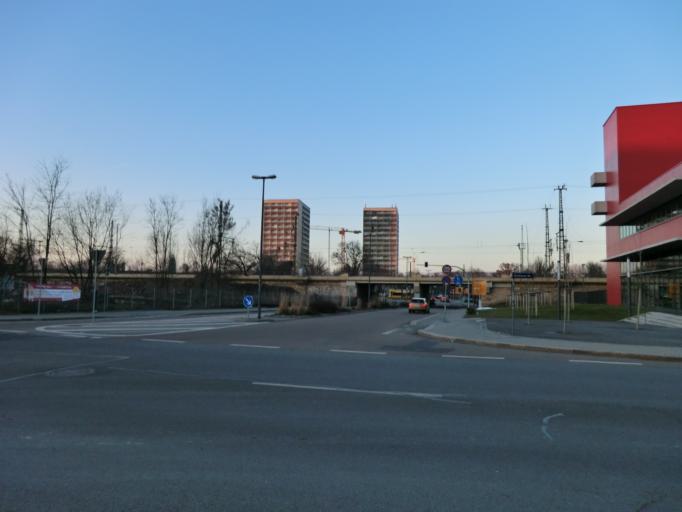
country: DE
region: Saxony
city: Dresden
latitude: 51.0355
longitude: 13.7437
